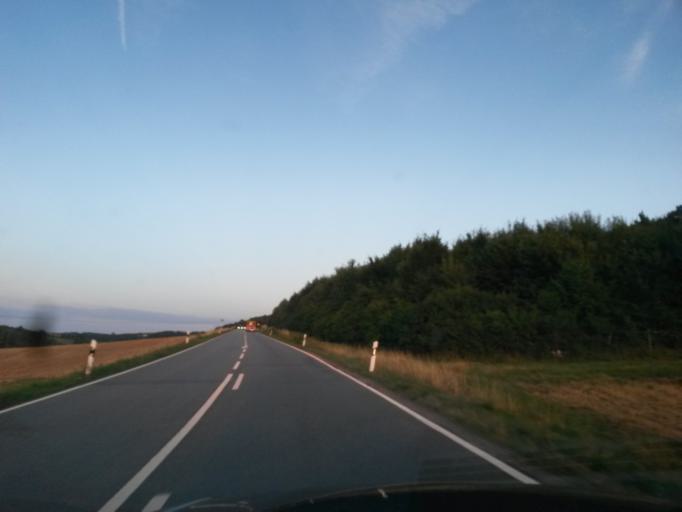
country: DE
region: Bavaria
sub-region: Regierungsbezirk Unterfranken
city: Marktheidenfeld
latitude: 49.8140
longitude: 9.6376
